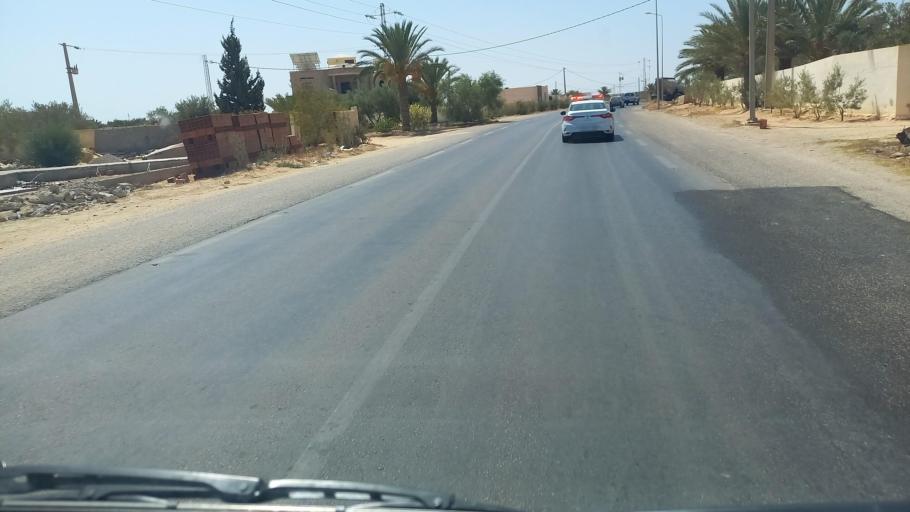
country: TN
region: Madanin
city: Houmt Souk
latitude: 33.7866
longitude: 10.8886
